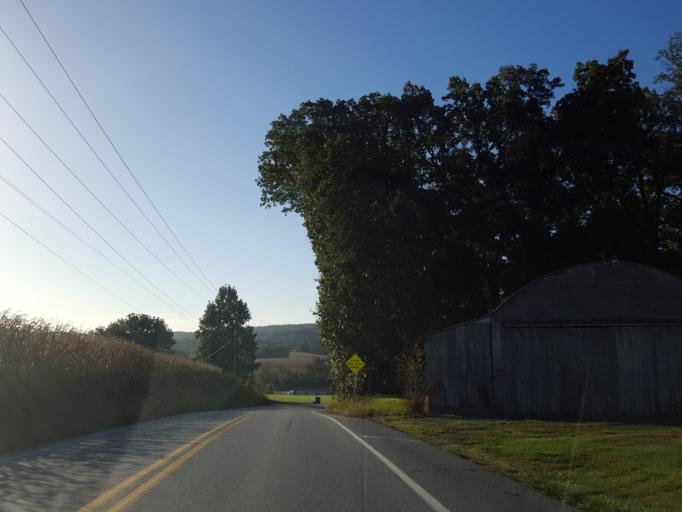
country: US
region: Pennsylvania
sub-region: York County
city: Stonybrook
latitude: 39.9646
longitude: -76.6127
